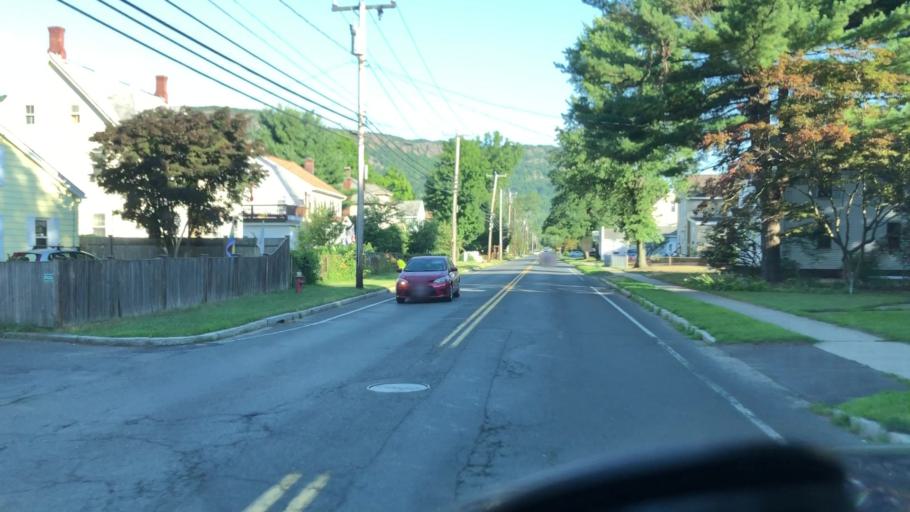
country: US
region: Massachusetts
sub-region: Hampshire County
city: Easthampton
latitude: 42.2623
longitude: -72.6624
